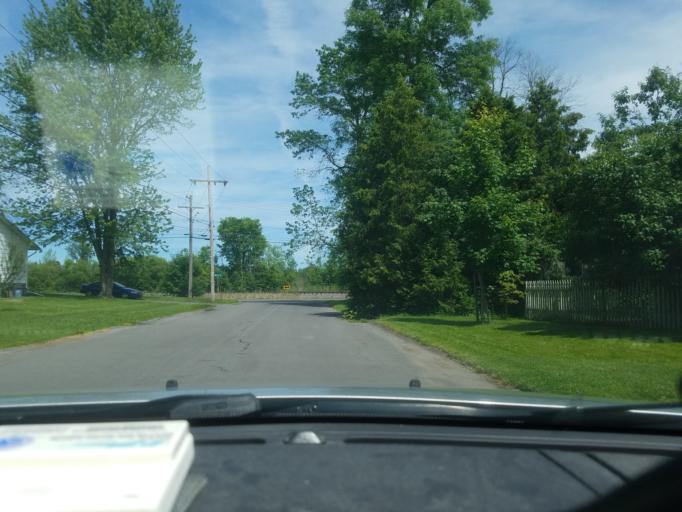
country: US
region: New York
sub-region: Onondaga County
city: East Syracuse
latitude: 43.0830
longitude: -76.0651
